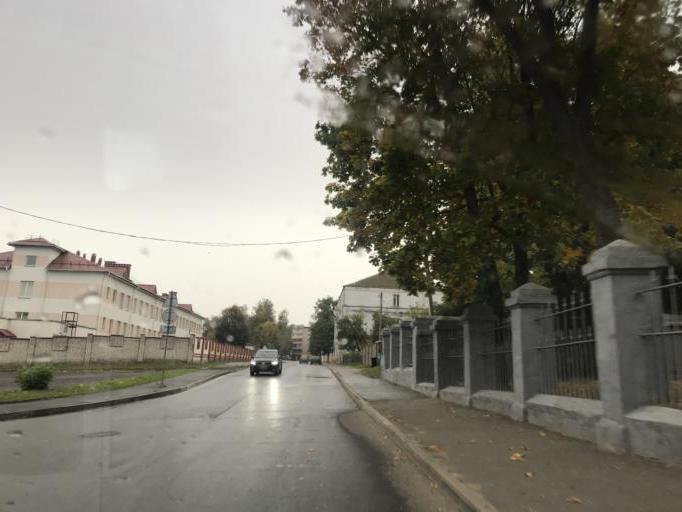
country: BY
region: Mogilev
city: Mahilyow
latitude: 53.8956
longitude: 30.3202
